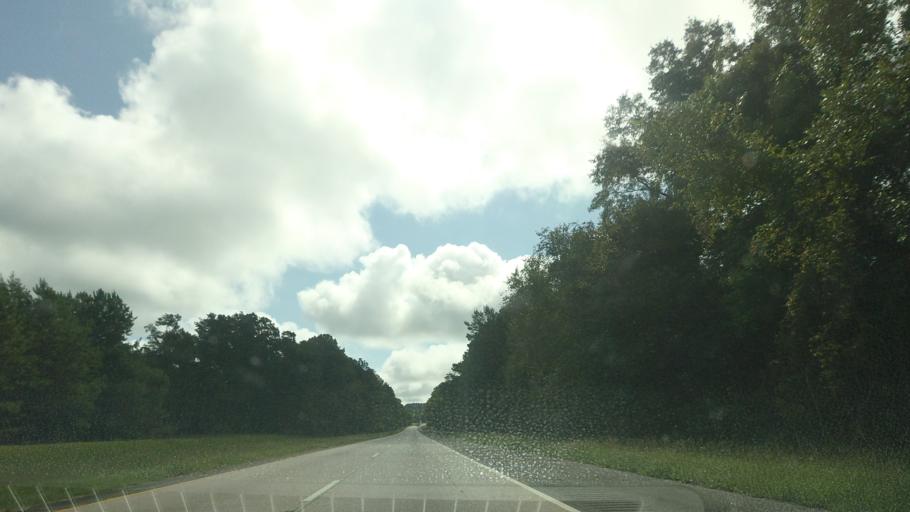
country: US
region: Georgia
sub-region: Twiggs County
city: Jeffersonville
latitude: 32.6496
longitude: -83.4219
